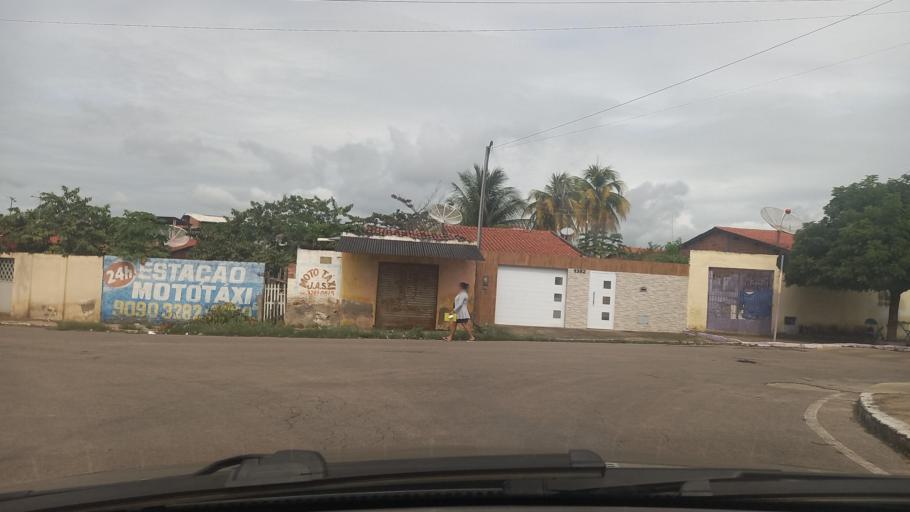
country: BR
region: Bahia
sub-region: Paulo Afonso
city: Paulo Afonso
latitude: -9.4383
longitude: -38.2115
